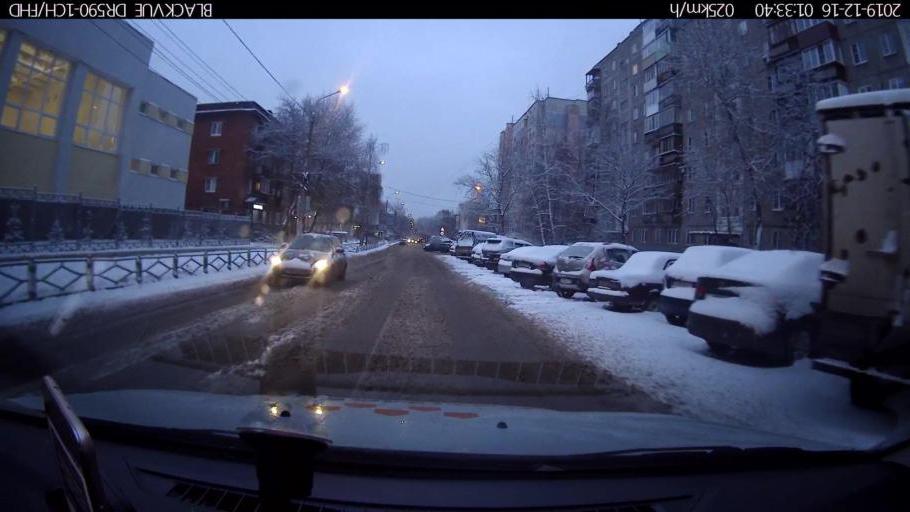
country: RU
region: Nizjnij Novgorod
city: Nizhniy Novgorod
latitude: 56.3091
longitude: 44.0284
